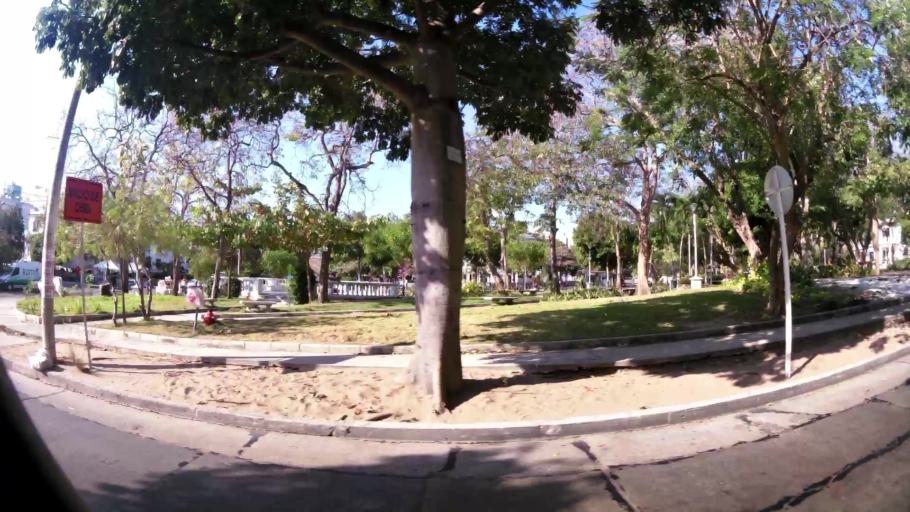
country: CO
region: Atlantico
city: Barranquilla
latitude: 10.9962
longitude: -74.7948
